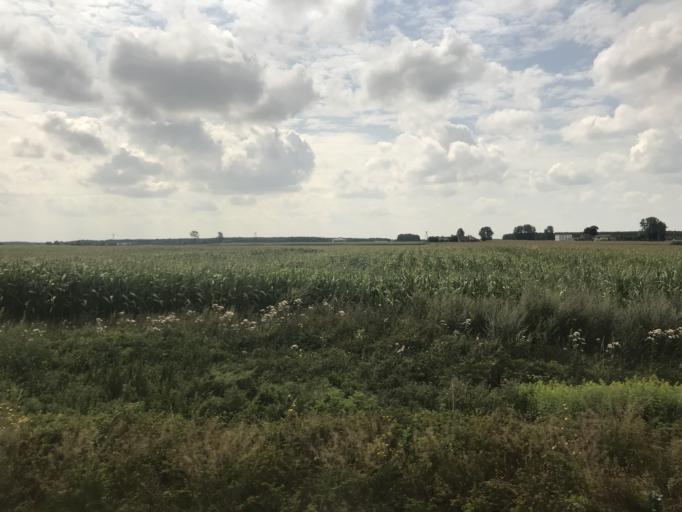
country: PL
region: Greater Poland Voivodeship
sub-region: Powiat gnieznienski
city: Lubowo
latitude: 52.5045
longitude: 17.4726
